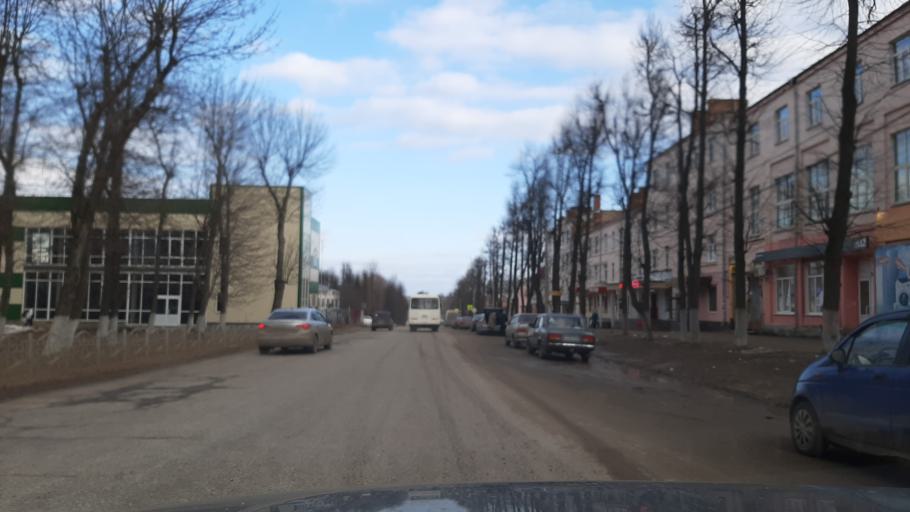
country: RU
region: Ivanovo
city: Teykovo
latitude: 56.8539
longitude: 40.5409
